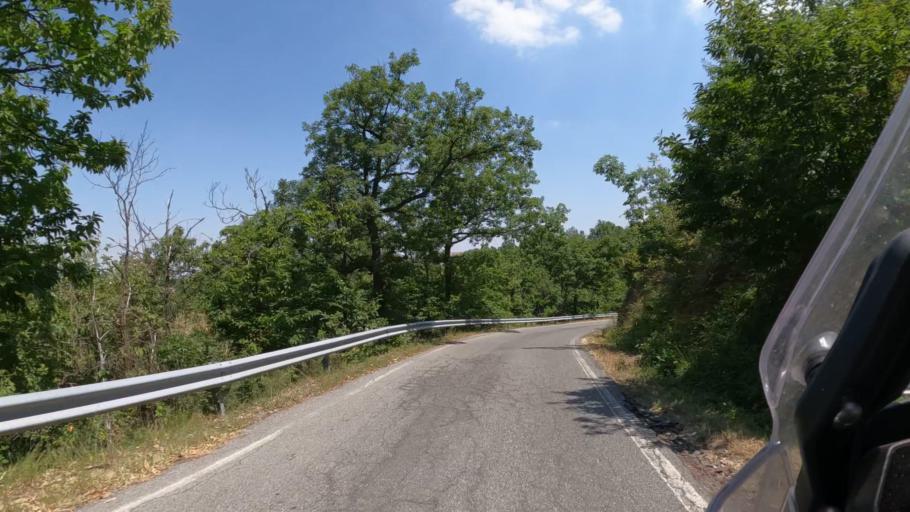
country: IT
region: Piedmont
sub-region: Provincia di Alessandria
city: Morbello
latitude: 44.5565
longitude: 8.5068
